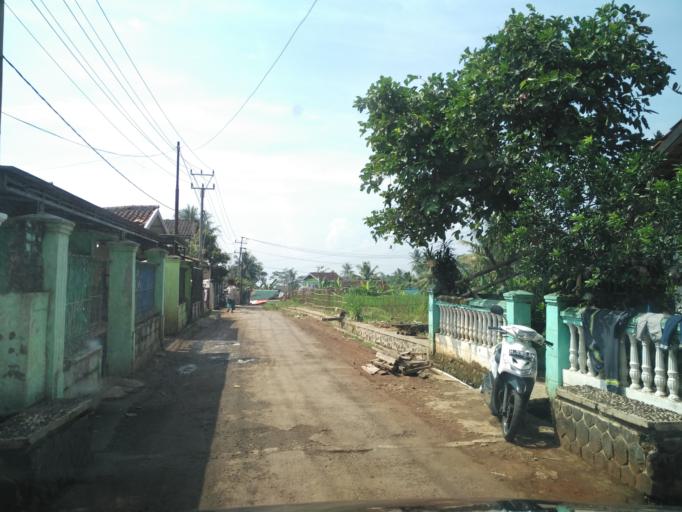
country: ID
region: West Java
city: Ciranjang-hilir
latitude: -6.7991
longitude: 107.1101
